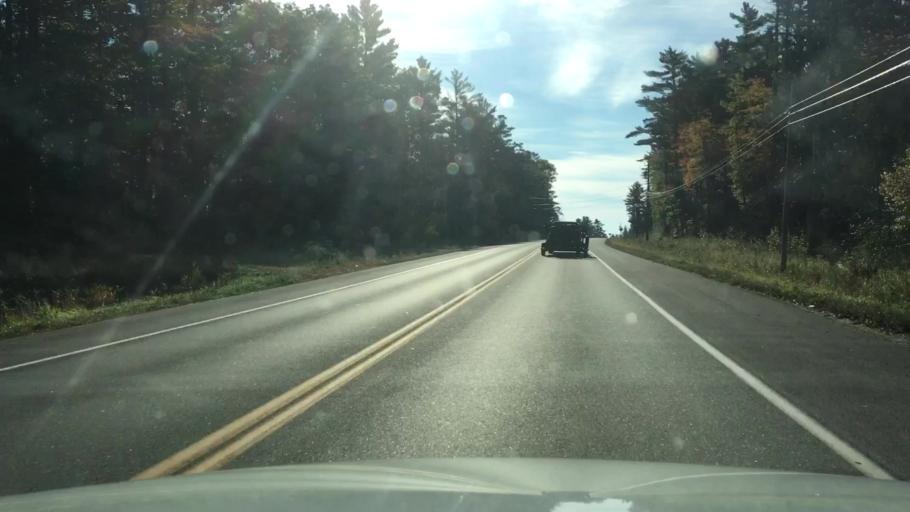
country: US
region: Maine
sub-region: Knox County
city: Warren
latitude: 44.0925
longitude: -69.2380
